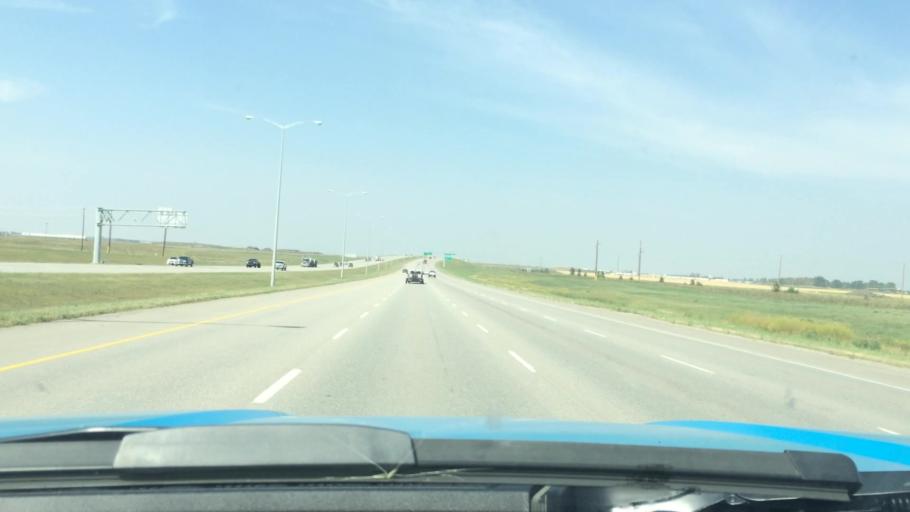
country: CA
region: Alberta
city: Chestermere
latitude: 50.9599
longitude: -113.9206
